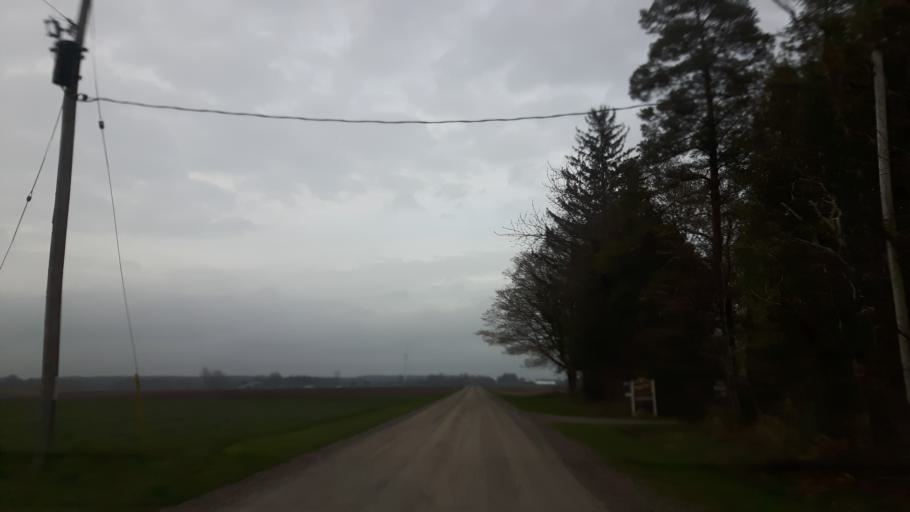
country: CA
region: Ontario
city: Bluewater
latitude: 43.5093
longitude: -81.6827
